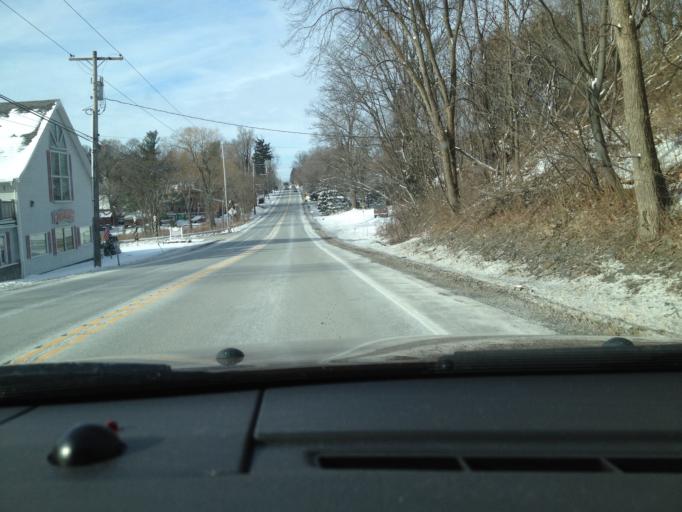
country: US
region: New York
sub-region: Rensselaer County
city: West Sand Lake
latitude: 42.6435
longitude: -73.6295
